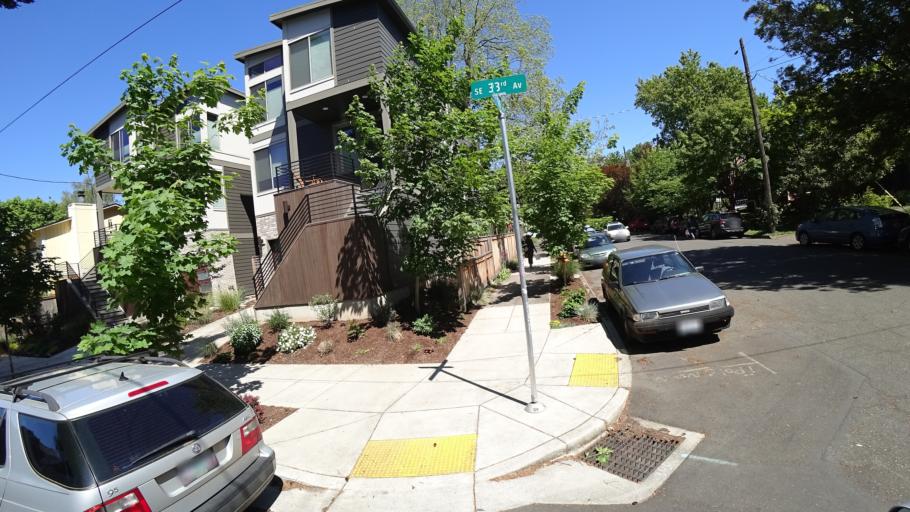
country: US
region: Oregon
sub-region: Multnomah County
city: Portland
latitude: 45.5130
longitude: -122.6308
